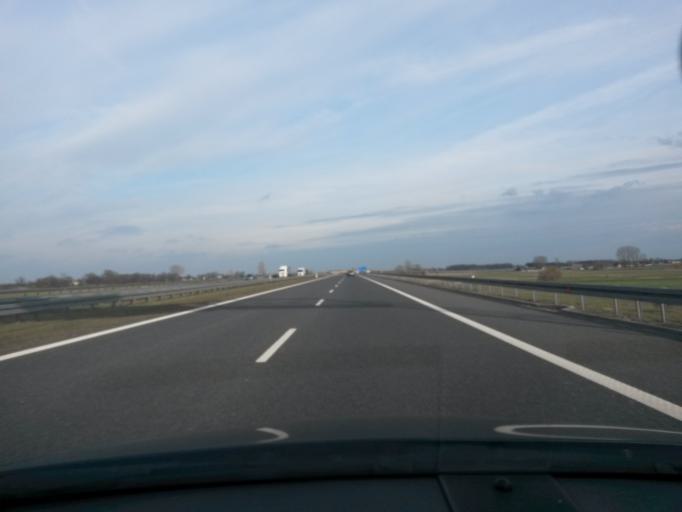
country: PL
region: Lodz Voivodeship
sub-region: Powiat poddebicki
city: Wartkowice
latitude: 51.9980
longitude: 19.0176
